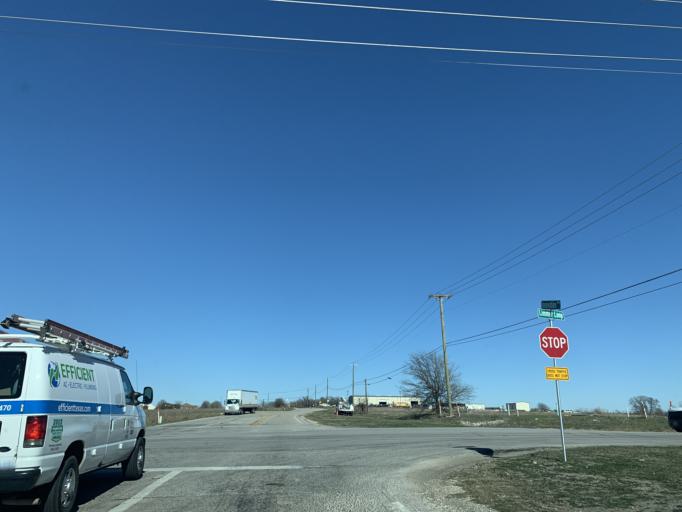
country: US
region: Texas
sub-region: Williamson County
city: Hutto
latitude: 30.5585
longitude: -97.5708
